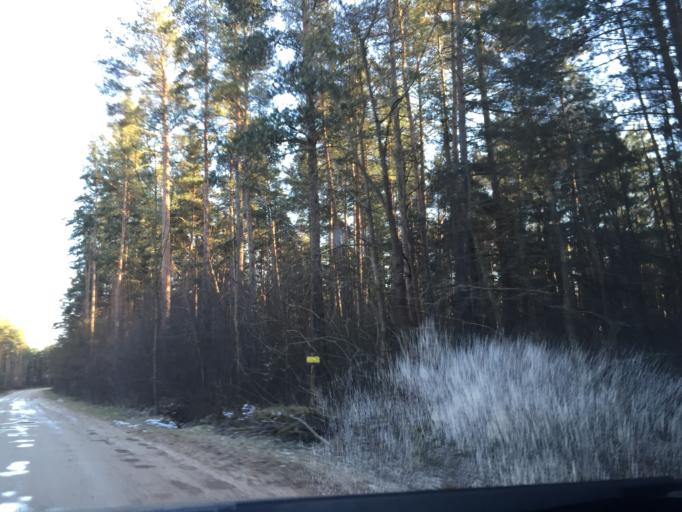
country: LV
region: Kekava
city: Kekava
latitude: 56.8681
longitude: 24.2032
